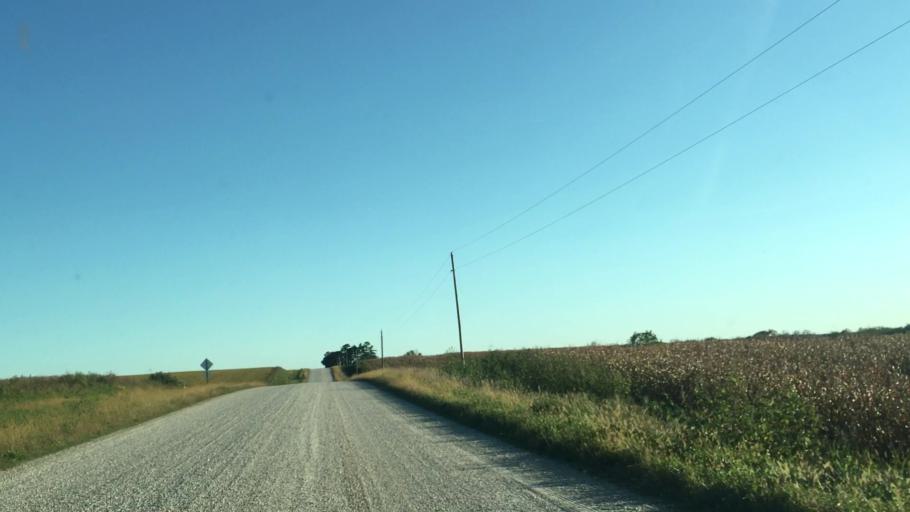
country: US
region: Minnesota
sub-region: Fillmore County
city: Preston
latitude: 43.8153
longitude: -92.0396
